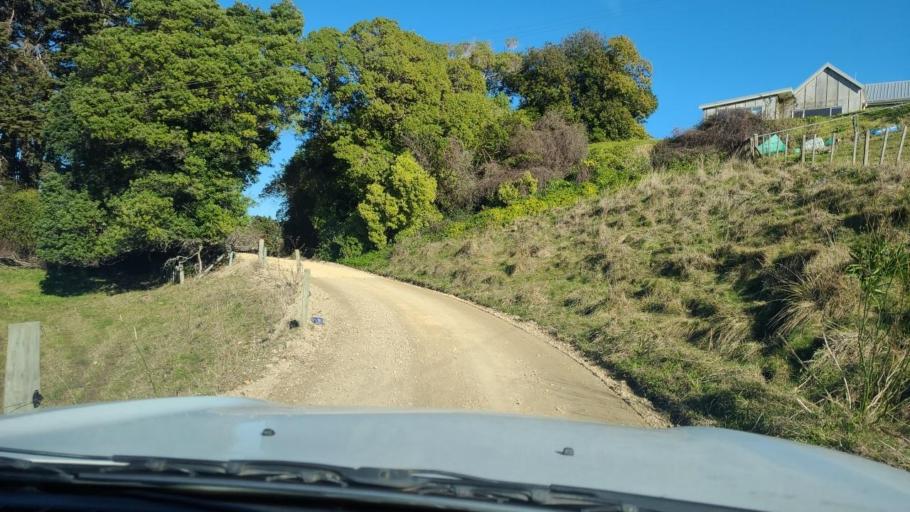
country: NZ
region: Hawke's Bay
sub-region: Hastings District
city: Hastings
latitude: -39.7930
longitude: 176.9731
